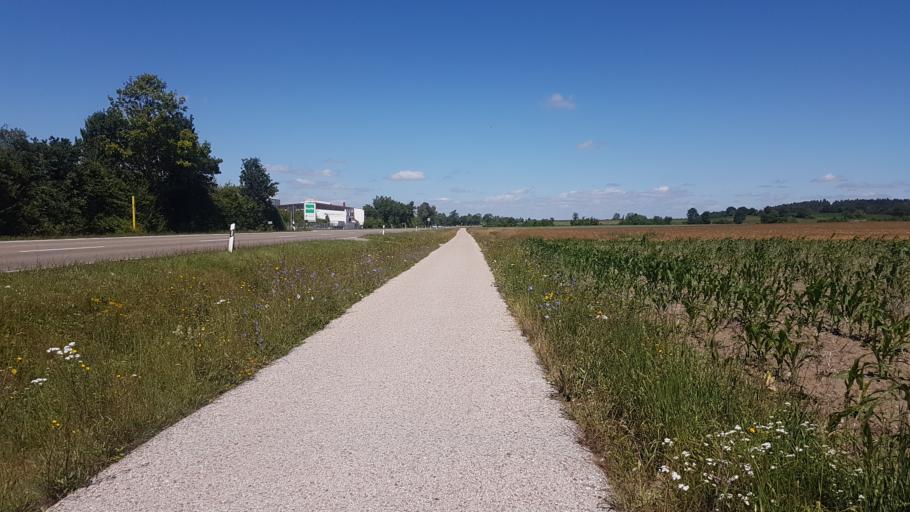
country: DE
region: Bavaria
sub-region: Regierungsbezirk Mittelfranken
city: Herrieden
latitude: 49.2390
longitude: 10.4768
